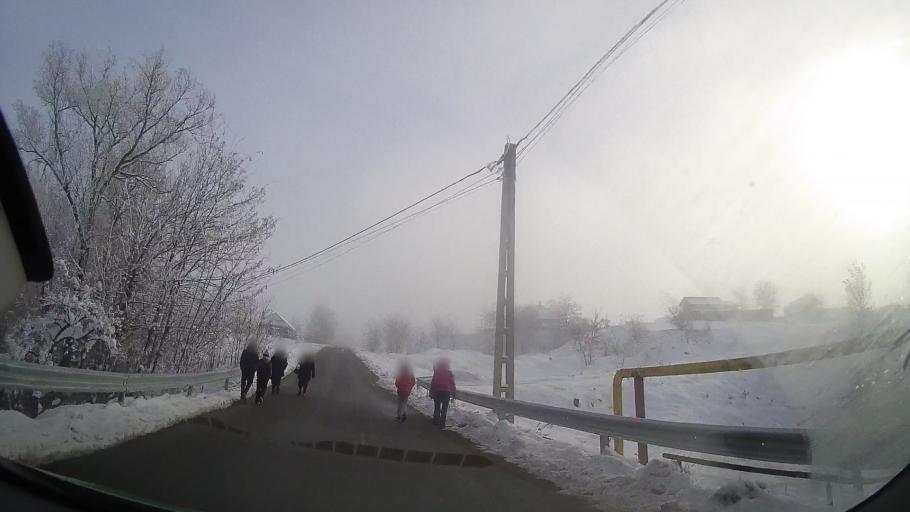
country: RO
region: Iasi
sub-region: Comuna Valea Seaca
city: Topile
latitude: 47.2467
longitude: 26.6611
